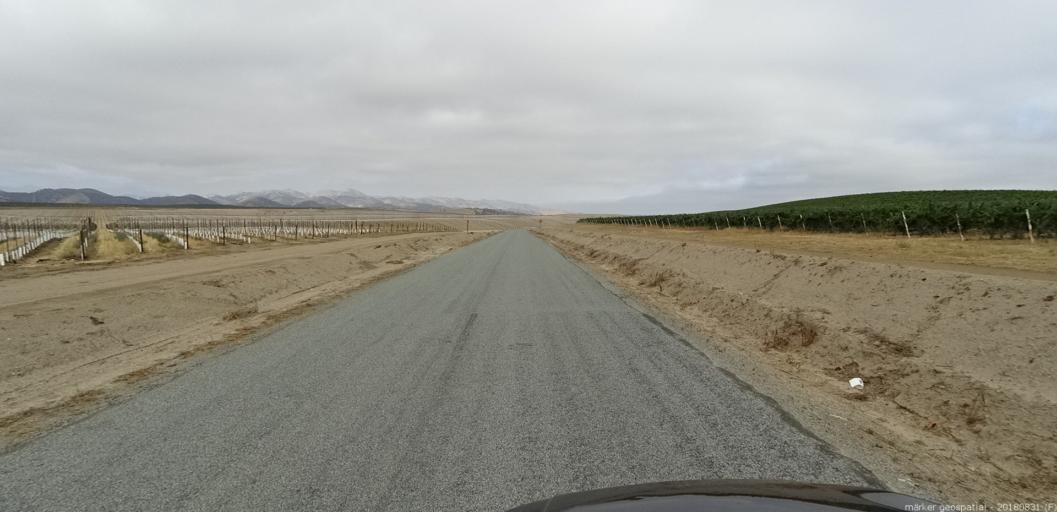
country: US
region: California
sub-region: Monterey County
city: King City
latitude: 36.1569
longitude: -121.1079
